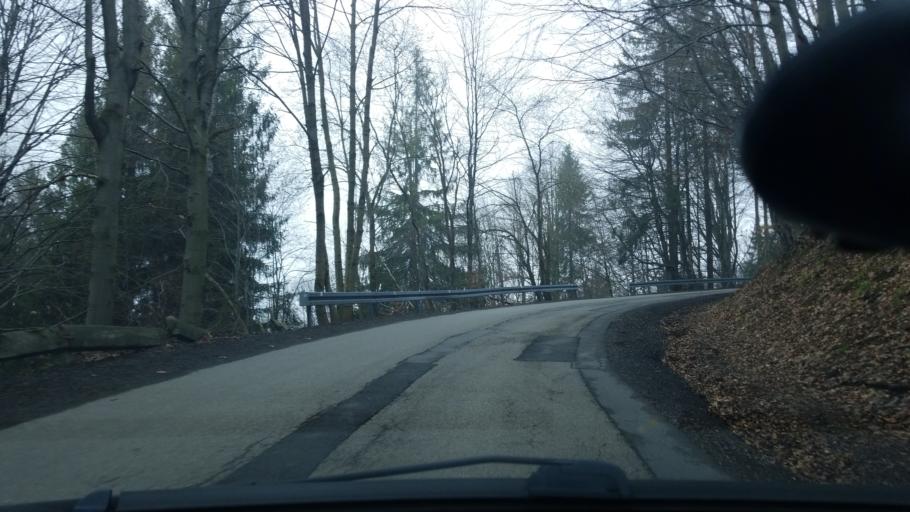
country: PL
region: Silesian Voivodeship
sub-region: Powiat cieszynski
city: Ustron
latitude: 49.7176
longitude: 18.8422
